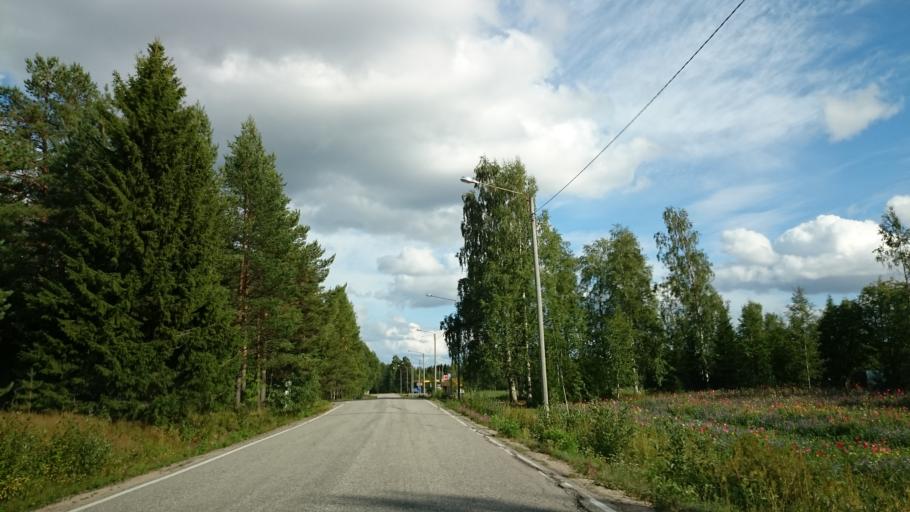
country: FI
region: Kainuu
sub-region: Kehys-Kainuu
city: Suomussalmi
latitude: 64.7467
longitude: 29.4425
